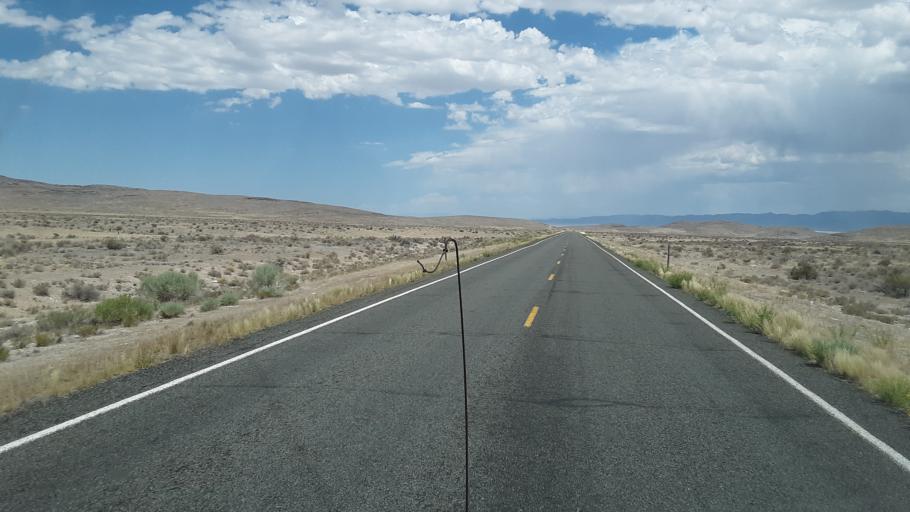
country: US
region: Utah
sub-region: Beaver County
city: Milford
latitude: 39.0368
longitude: -113.3333
